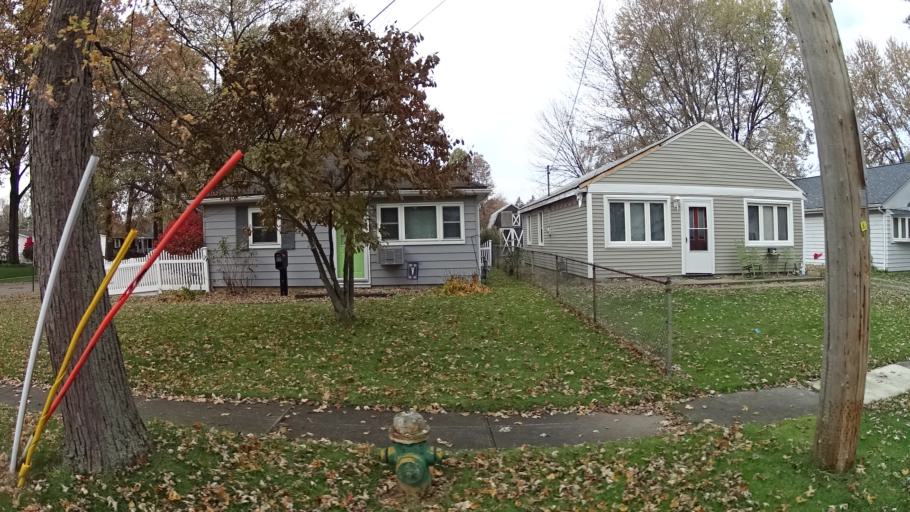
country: US
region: Ohio
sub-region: Lorain County
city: Elyria
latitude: 41.3598
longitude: -82.0805
